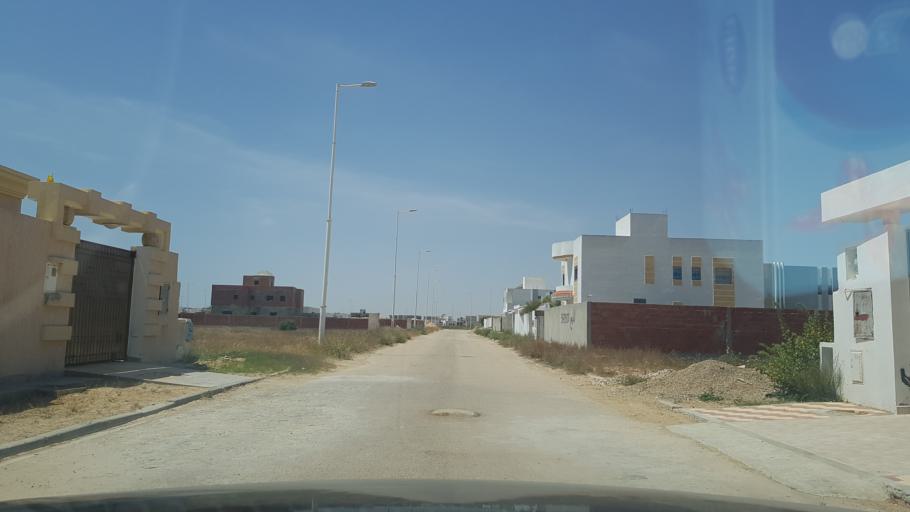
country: TN
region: Safaqis
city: Al Qarmadah
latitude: 34.8355
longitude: 10.7568
